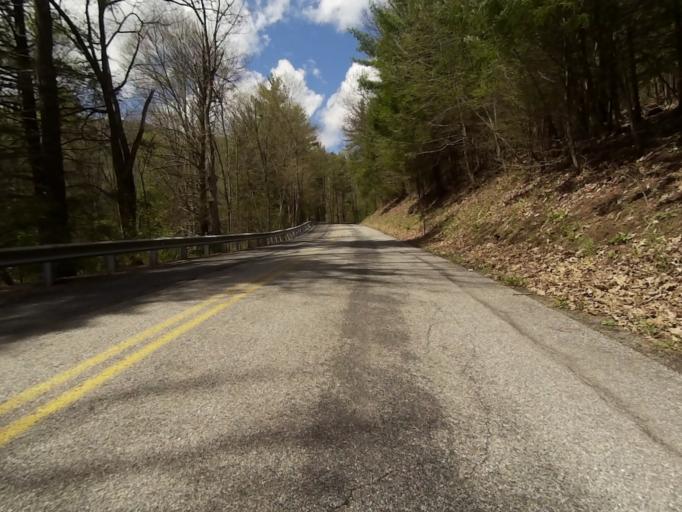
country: US
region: Pennsylvania
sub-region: Centre County
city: Milesburg
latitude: 40.9540
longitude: -77.8902
